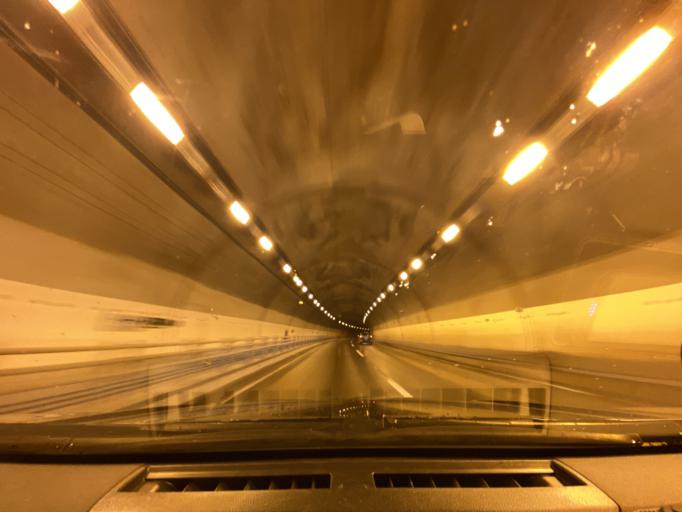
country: JP
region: Hokkaido
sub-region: Asahikawa-shi
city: Asahikawa
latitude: 43.8023
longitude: 142.3439
